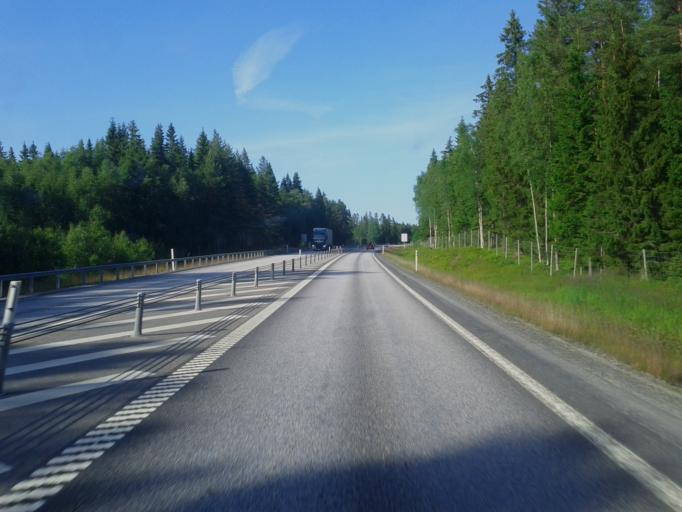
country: SE
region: Vaesterbotten
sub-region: Umea Kommun
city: Saevar
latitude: 63.9149
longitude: 20.5959
